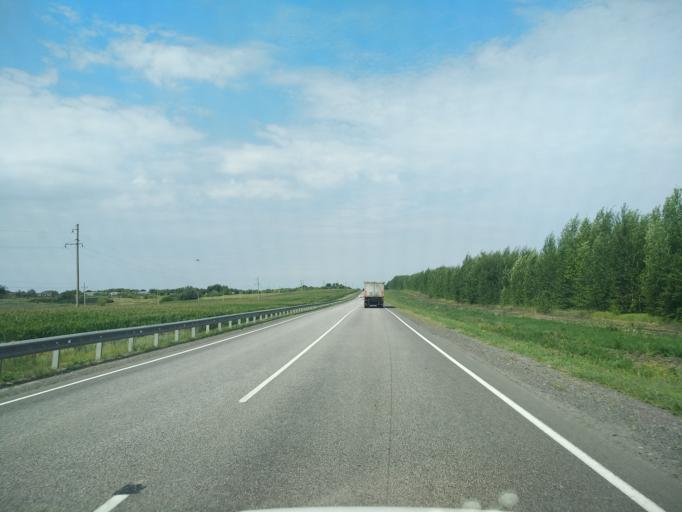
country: RU
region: Voronezj
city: Orlovo
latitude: 51.6759
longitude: 39.7264
